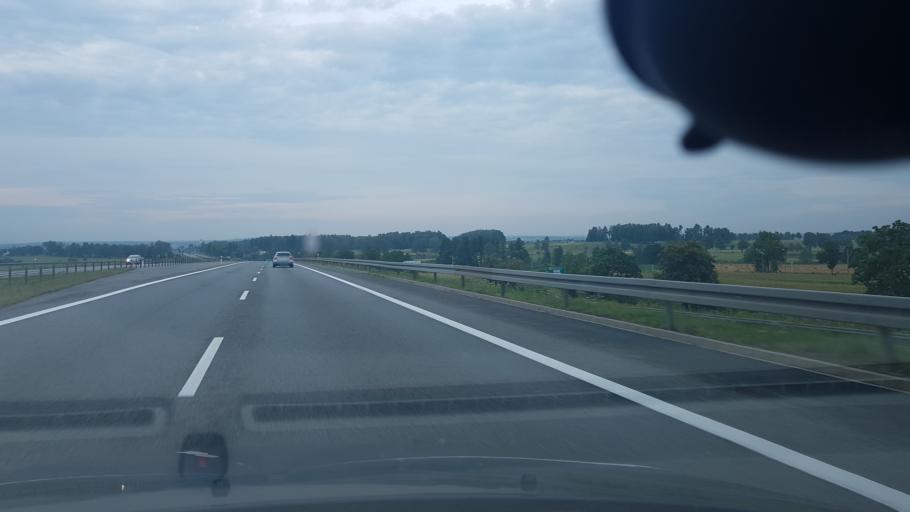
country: PL
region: Warmian-Masurian Voivodeship
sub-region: Powiat elblaski
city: Paslek
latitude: 54.0647
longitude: 19.6244
